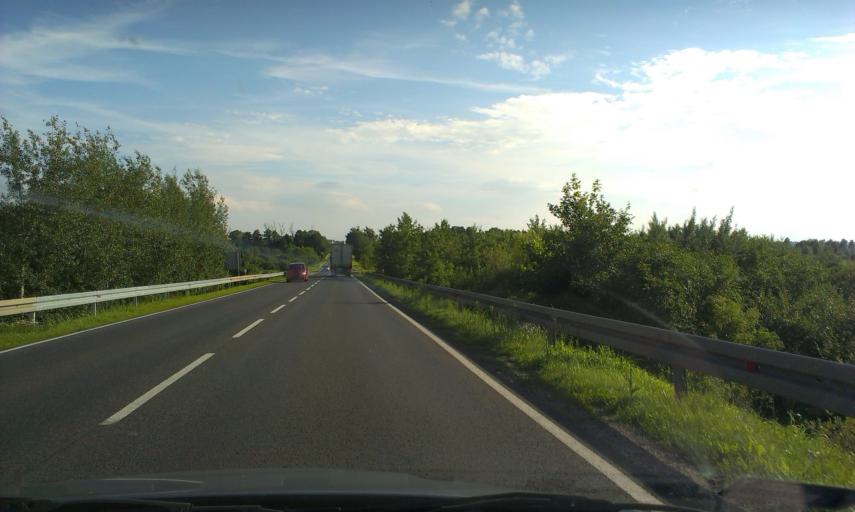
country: PL
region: Kujawsko-Pomorskie
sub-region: Powiat bydgoski
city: Biale Blota
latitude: 53.1507
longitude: 17.8851
